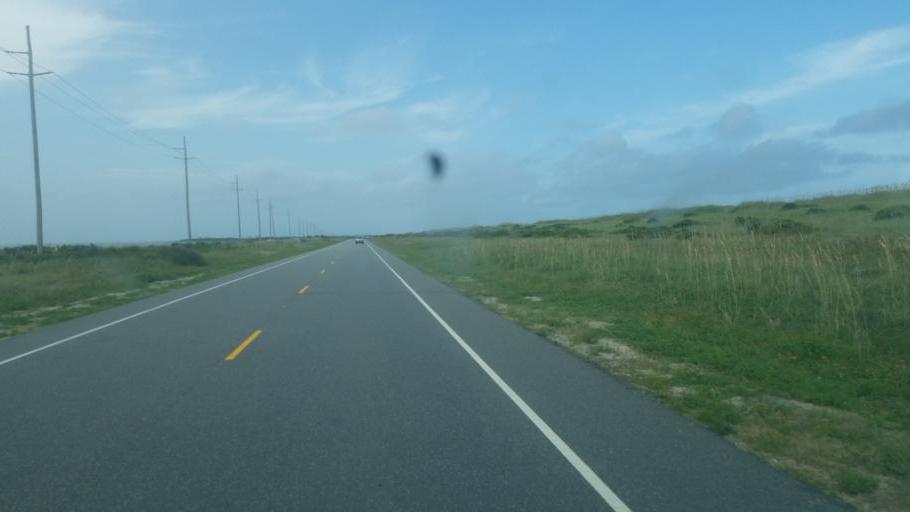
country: US
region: North Carolina
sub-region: Dare County
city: Buxton
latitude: 35.2933
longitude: -75.5146
